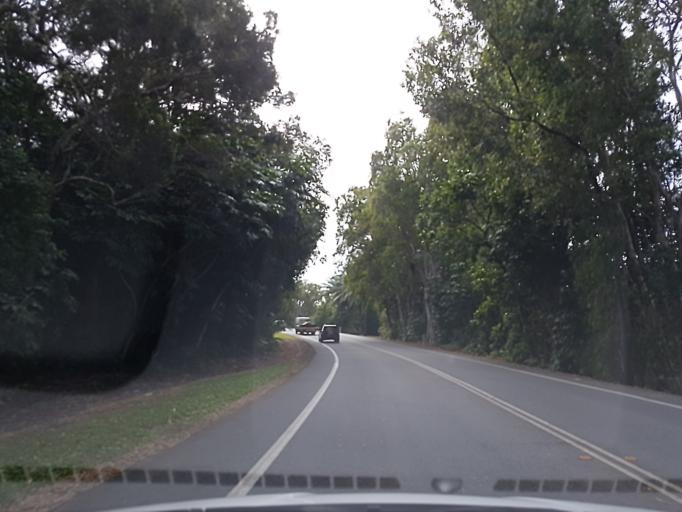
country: AU
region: Queensland
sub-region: Cairns
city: Port Douglas
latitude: -16.5246
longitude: 145.4668
